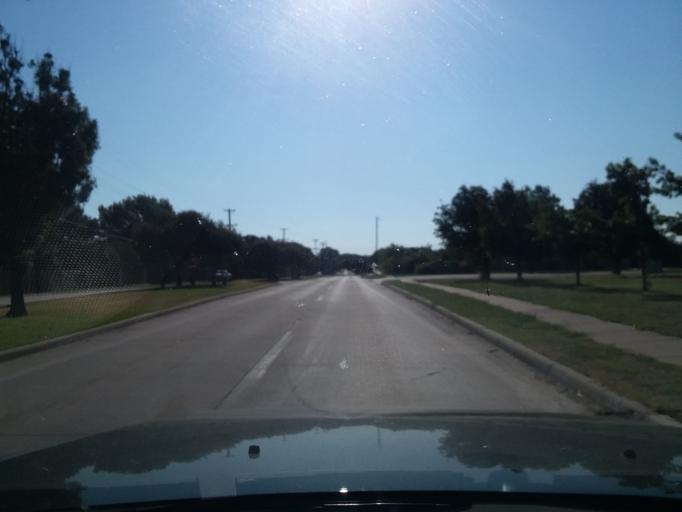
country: US
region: Texas
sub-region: Denton County
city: Highland Village
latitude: 33.0496
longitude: -97.0472
